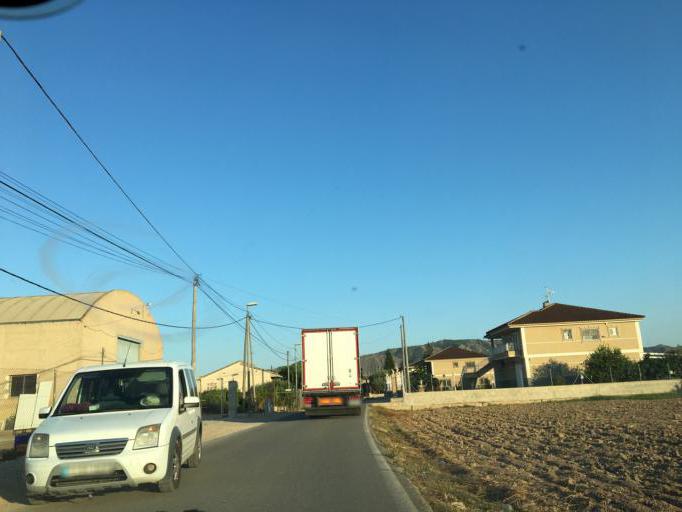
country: ES
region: Murcia
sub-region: Murcia
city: Santomera
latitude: 38.0146
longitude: -1.0575
